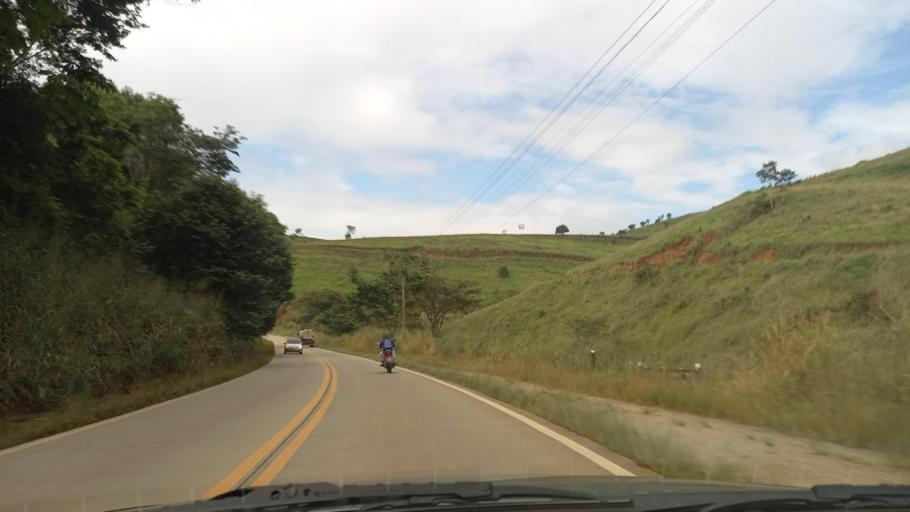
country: BR
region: Pernambuco
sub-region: Maraial
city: Maraial
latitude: -8.7461
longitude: -35.8026
